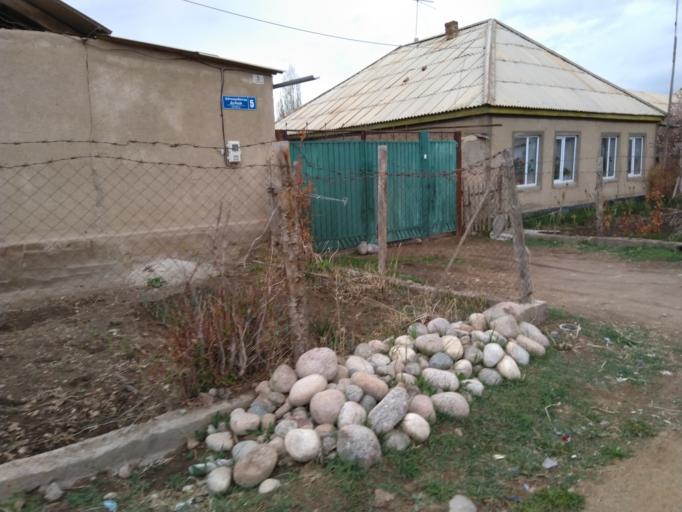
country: KG
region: Ysyk-Koel
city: Bokombayevskoye
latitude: 42.1083
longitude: 76.9823
